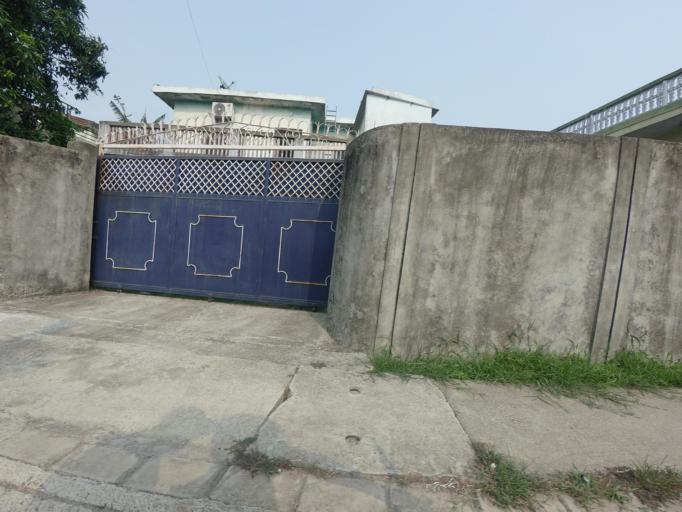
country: NP
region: Western Region
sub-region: Lumbini Zone
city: Bhairahawa
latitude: 27.5252
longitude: 83.4588
